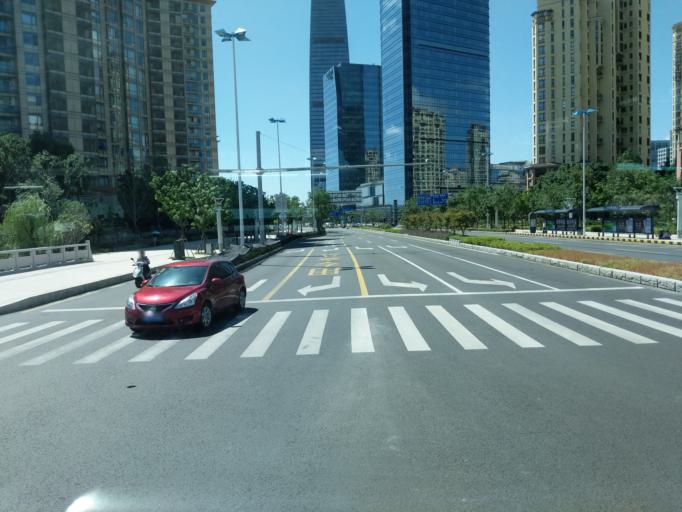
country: CN
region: Jiangsu Sheng
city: Weiting
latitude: 31.3246
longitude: 120.6738
